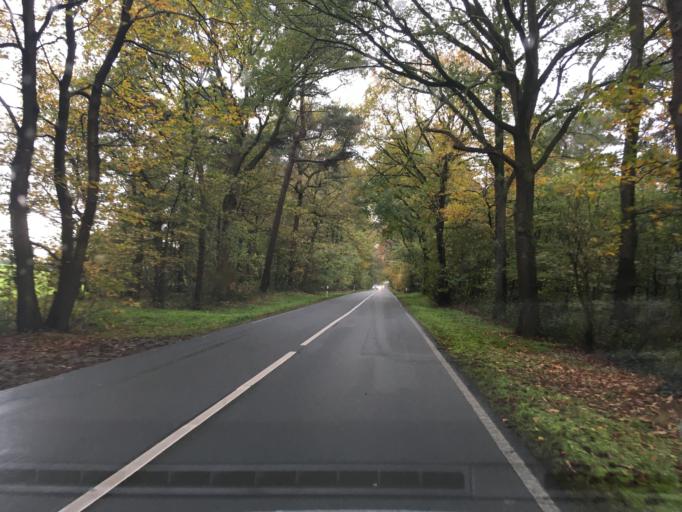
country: DE
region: North Rhine-Westphalia
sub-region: Regierungsbezirk Munster
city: Heiden
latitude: 51.8235
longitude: 6.9823
